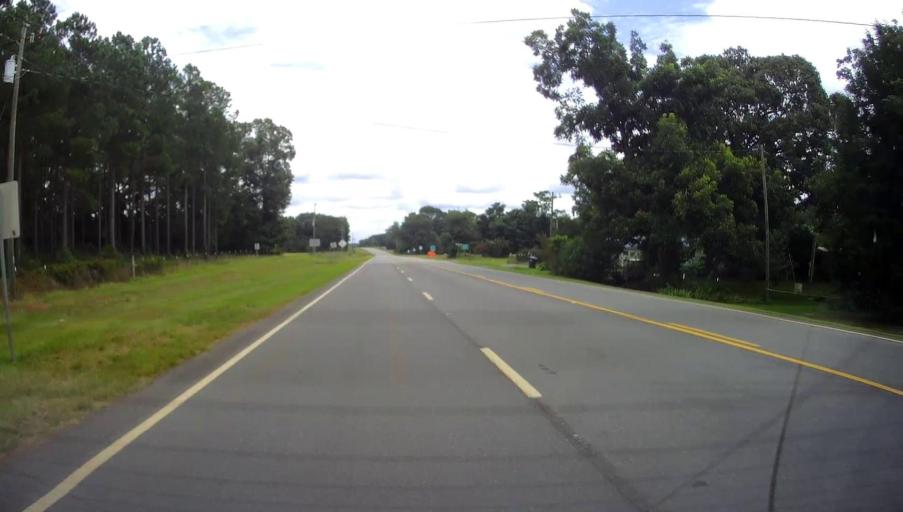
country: US
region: Georgia
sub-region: Schley County
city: Ellaville
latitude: 32.2597
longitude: -84.2203
